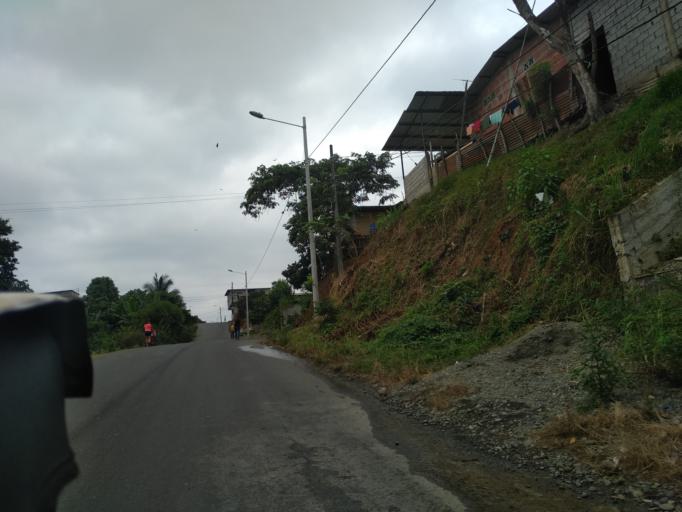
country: EC
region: Los Rios
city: Quevedo
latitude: -1.0233
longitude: -79.4403
